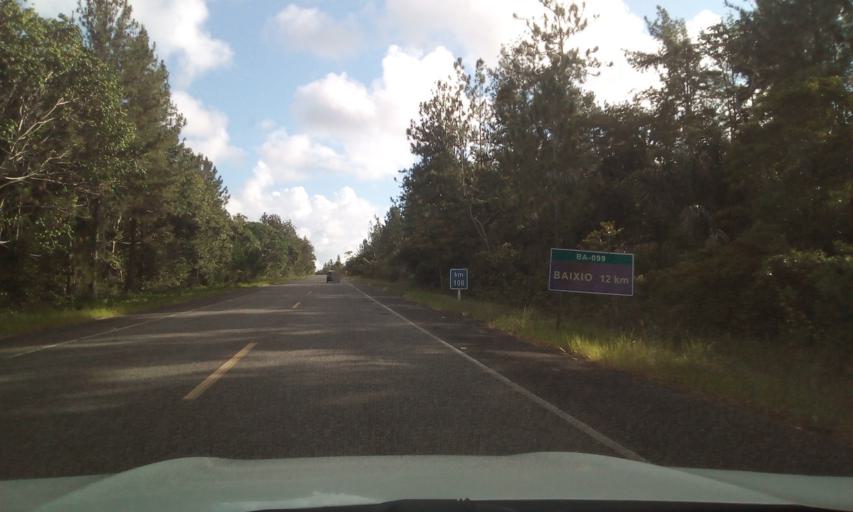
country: BR
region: Bahia
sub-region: Entre Rios
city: Entre Rios
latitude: -12.1462
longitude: -37.7955
